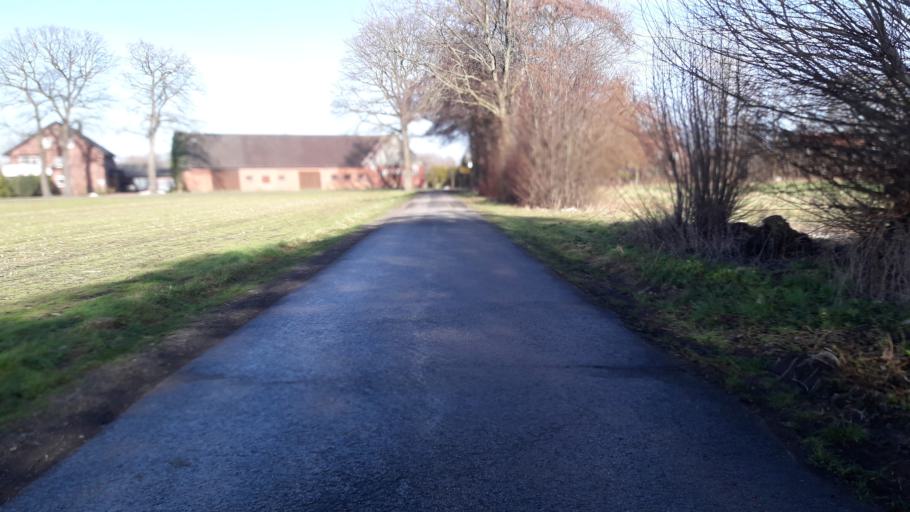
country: DE
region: North Rhine-Westphalia
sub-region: Regierungsbezirk Detmold
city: Delbruck
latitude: 51.7435
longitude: 8.5016
